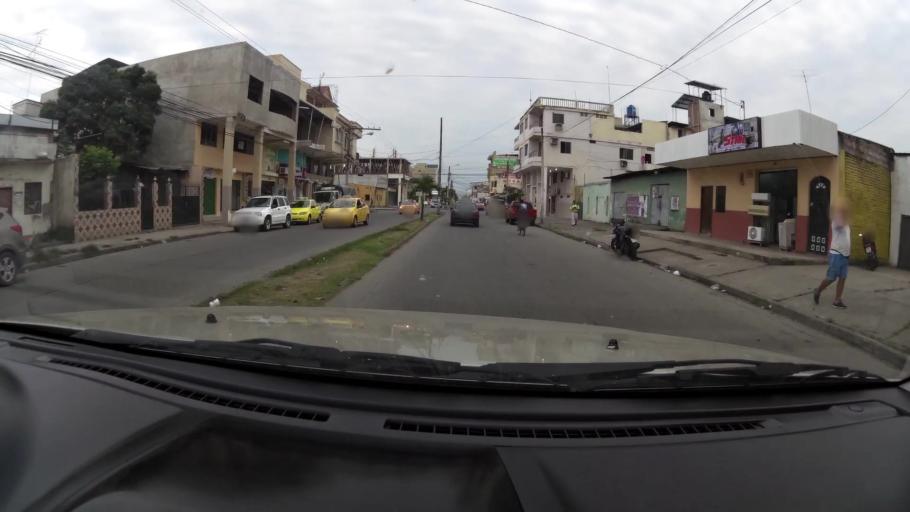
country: EC
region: El Oro
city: Machala
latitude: -3.2540
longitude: -79.9551
